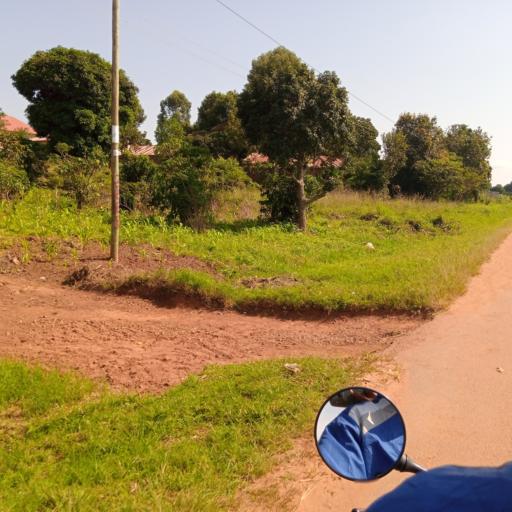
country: UG
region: Central Region
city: Masaka
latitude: -0.3671
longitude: 31.7167
